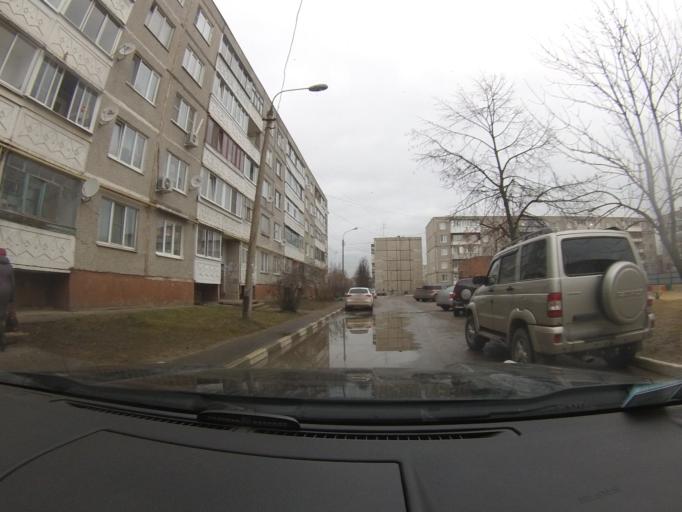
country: RU
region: Moskovskaya
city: Lopatinskiy
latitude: 55.3351
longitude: 38.7109
